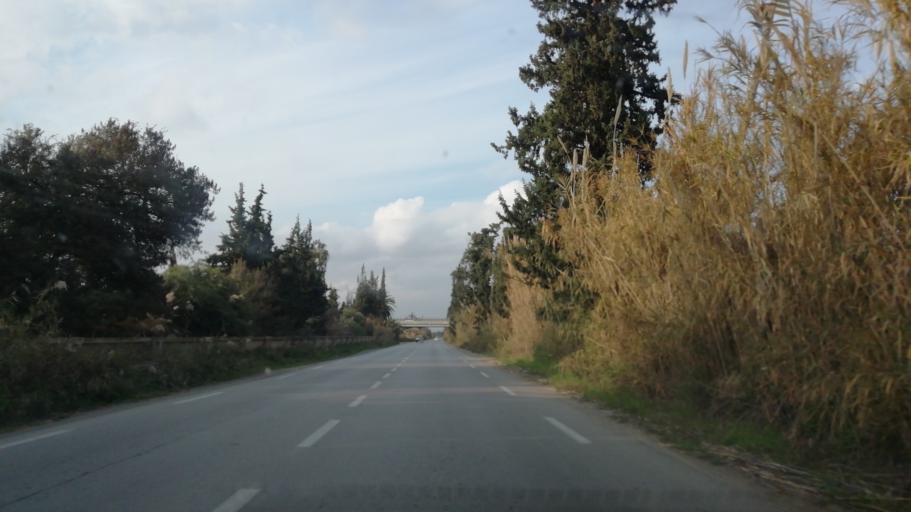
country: DZ
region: Mascara
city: Mascara
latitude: 35.6187
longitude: 0.0476
